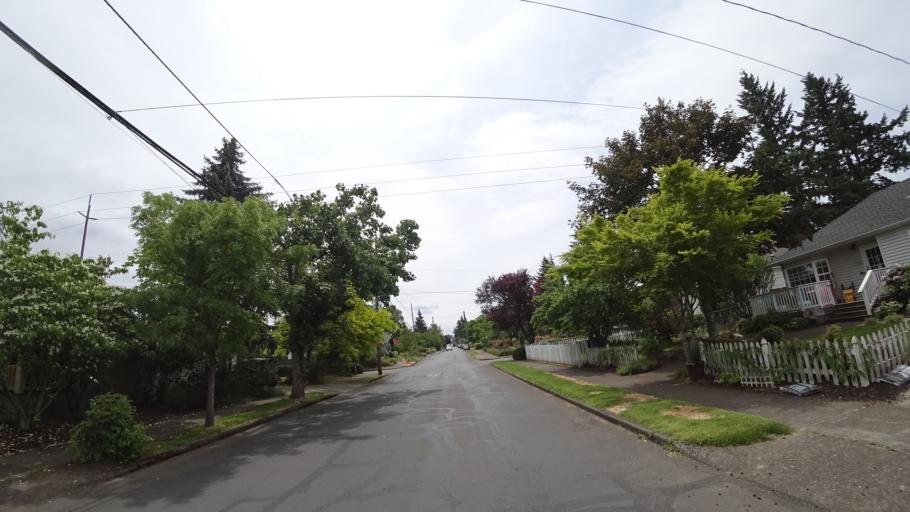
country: US
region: Oregon
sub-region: Multnomah County
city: Portland
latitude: 45.5617
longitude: -122.6256
